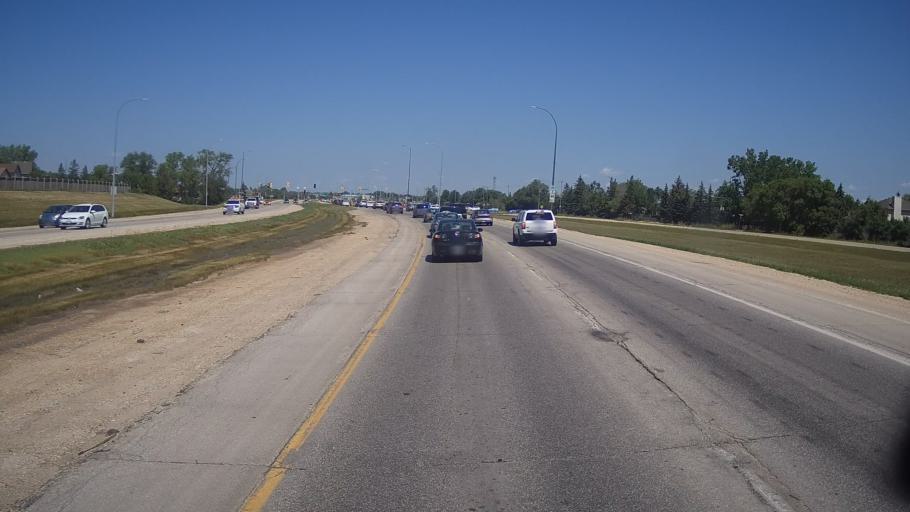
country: CA
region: Manitoba
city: Winnipeg
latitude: 49.9200
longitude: -97.0485
